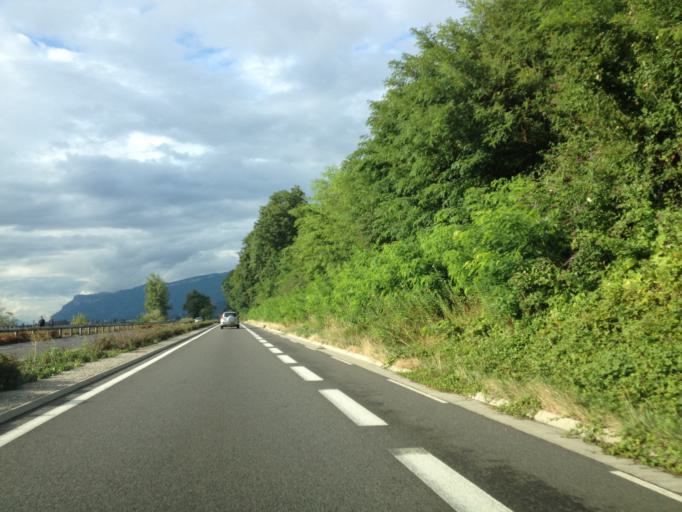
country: FR
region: Rhone-Alpes
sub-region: Departement de la Savoie
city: Tresserve
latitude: 45.6714
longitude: 5.8936
